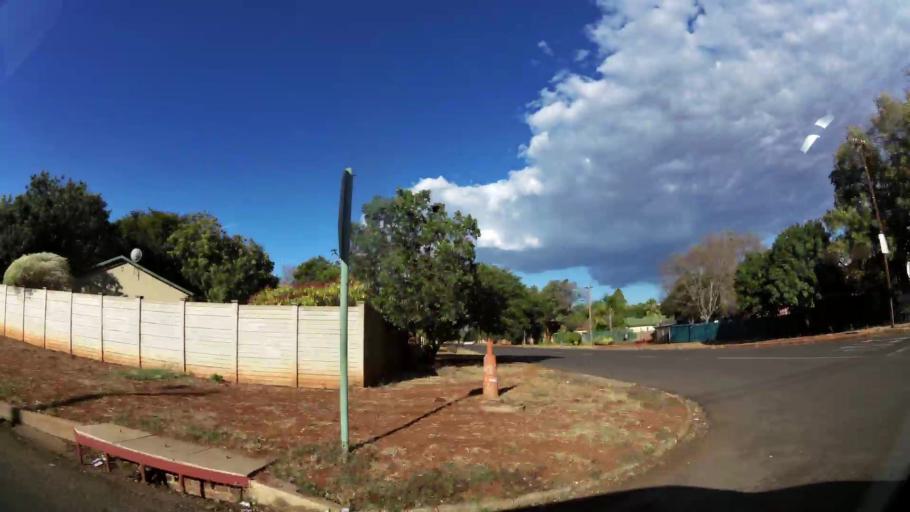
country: ZA
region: Limpopo
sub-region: Waterberg District Municipality
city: Mokopane
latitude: -24.1851
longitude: 28.9990
